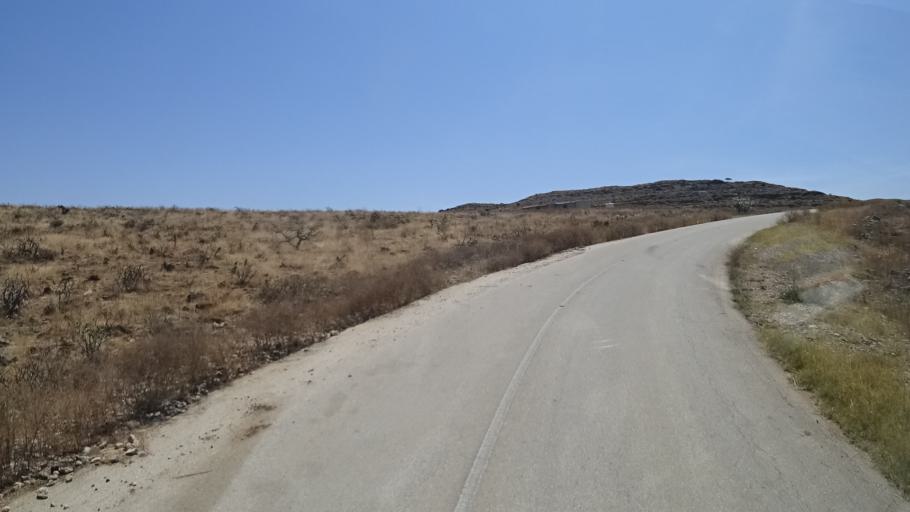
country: OM
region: Zufar
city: Salalah
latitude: 17.1549
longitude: 54.6217
